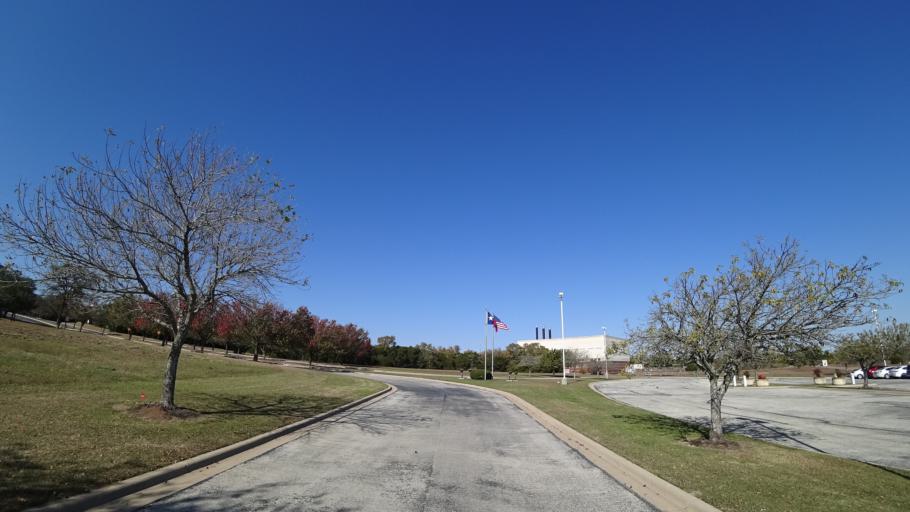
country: US
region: Texas
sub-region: Williamson County
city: Anderson Mill
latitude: 30.3952
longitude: -97.8429
